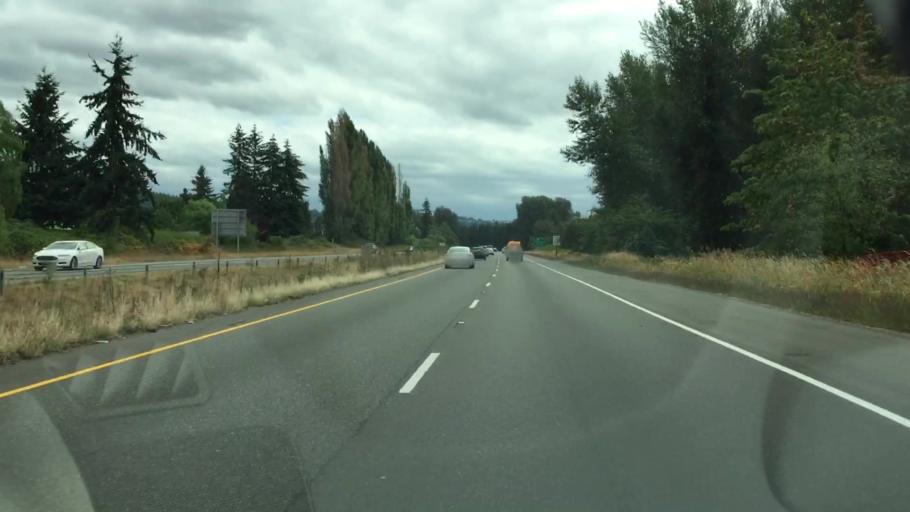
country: US
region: Washington
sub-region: Pierce County
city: Sumner
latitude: 47.1960
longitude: -122.2456
